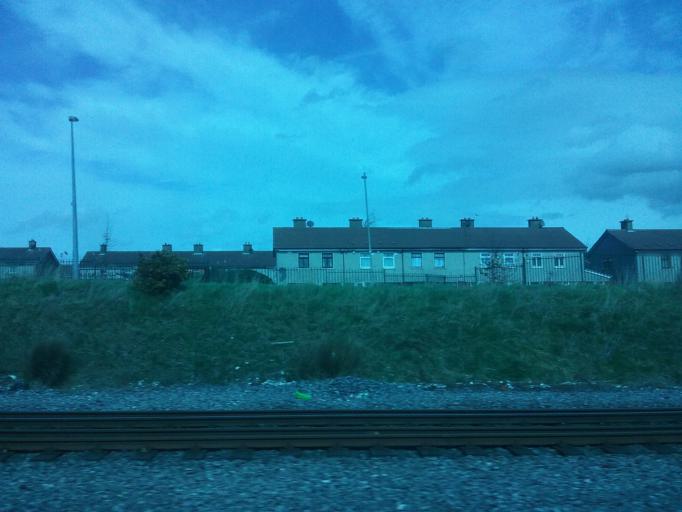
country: IE
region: Leinster
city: Ballyfermot
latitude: 53.3351
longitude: -6.3642
